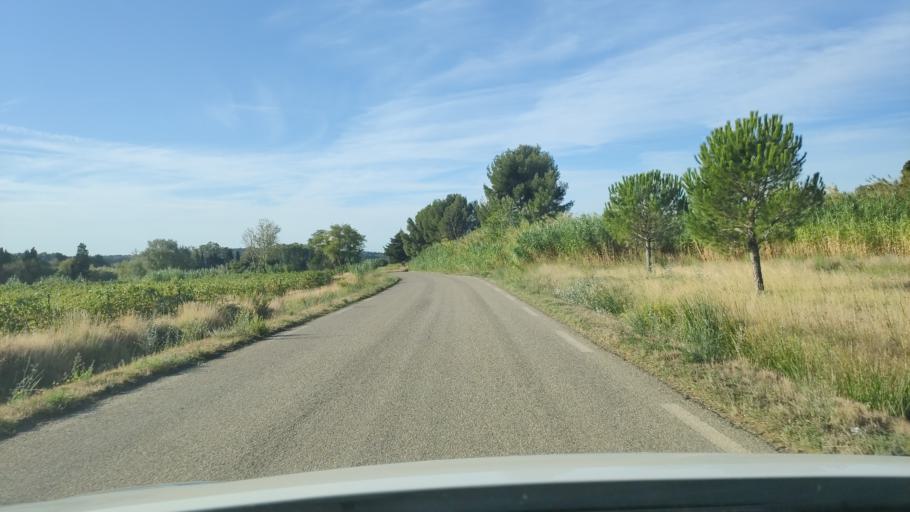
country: FR
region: Languedoc-Roussillon
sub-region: Departement du Gard
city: Saze
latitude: 43.9453
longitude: 4.6536
